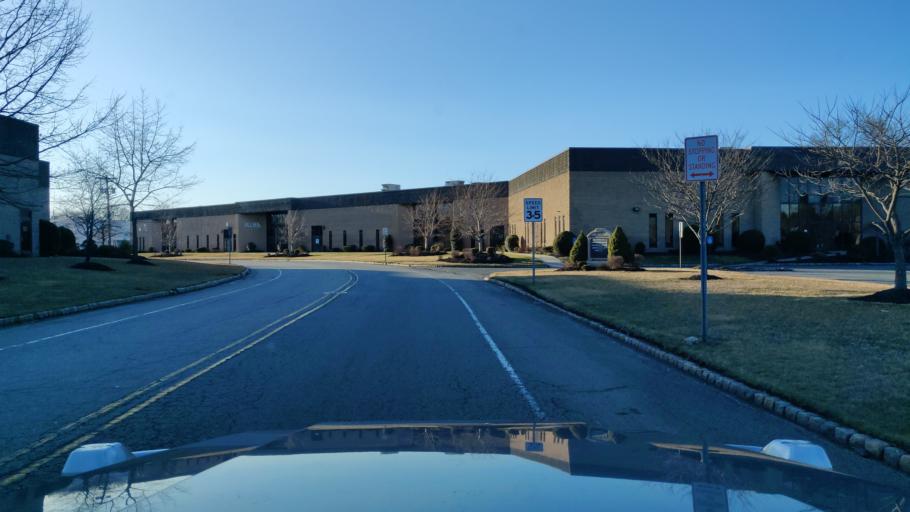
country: US
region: New Jersey
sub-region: Essex County
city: Fairfield
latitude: 40.8715
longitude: -74.3064
